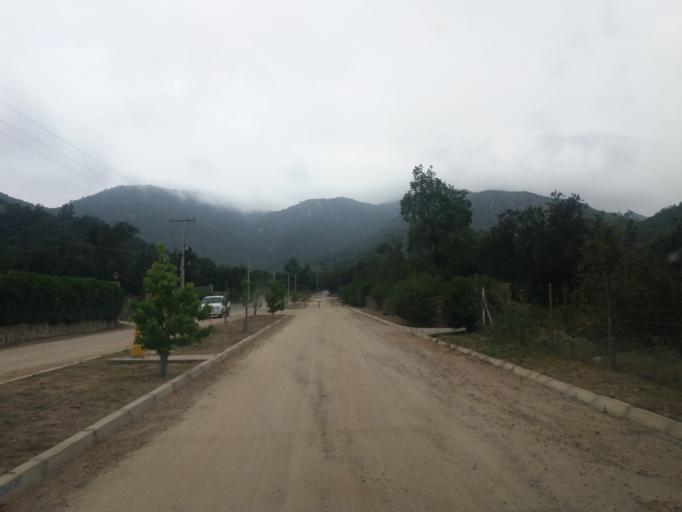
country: CL
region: Valparaiso
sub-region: Provincia de Marga Marga
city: Limache
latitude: -33.0258
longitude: -71.1311
